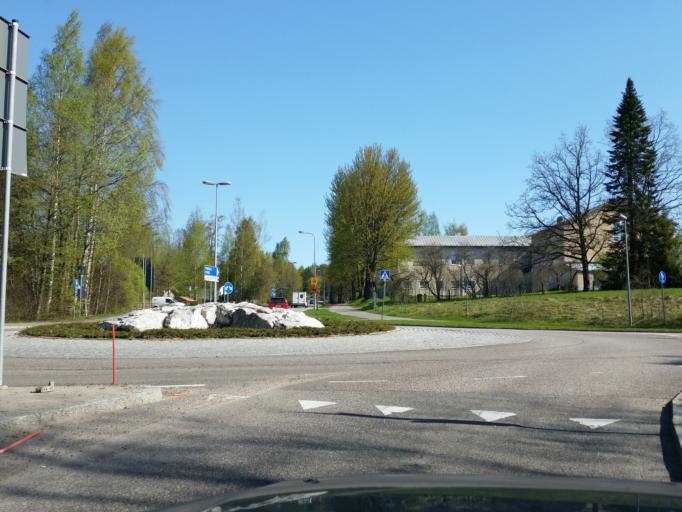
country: FI
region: Uusimaa
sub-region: Helsinki
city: Lohja
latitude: 60.1794
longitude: 23.9910
